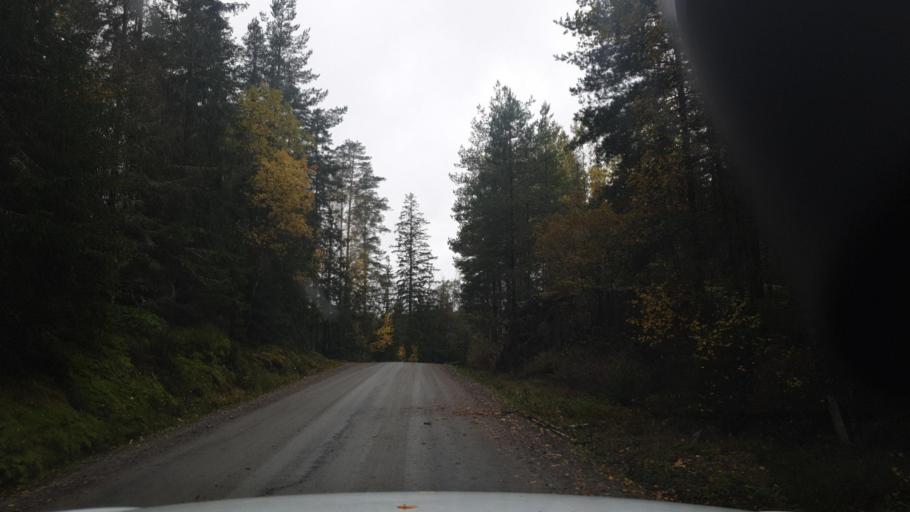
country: SE
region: Vaermland
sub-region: Karlstads Kommun
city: Edsvalla
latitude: 59.4413
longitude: 13.1870
